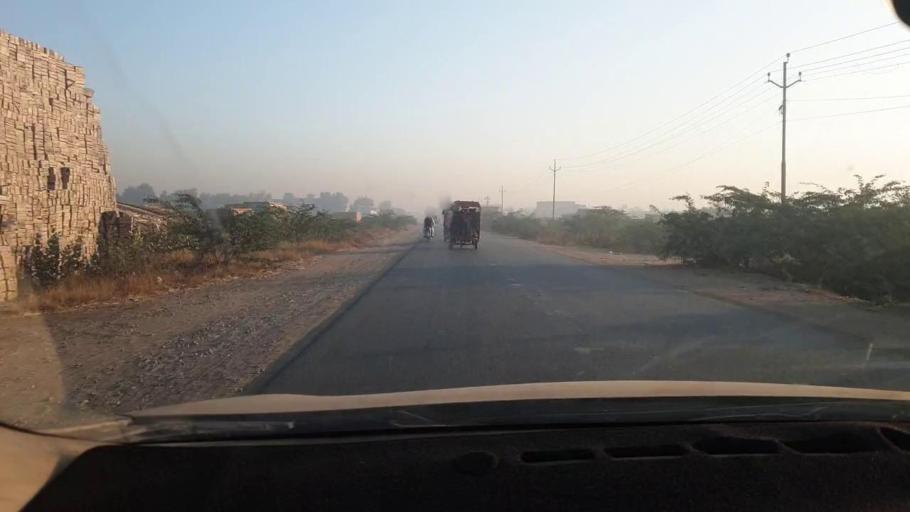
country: PK
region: Sindh
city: Malir Cantonment
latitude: 25.0003
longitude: 67.1476
